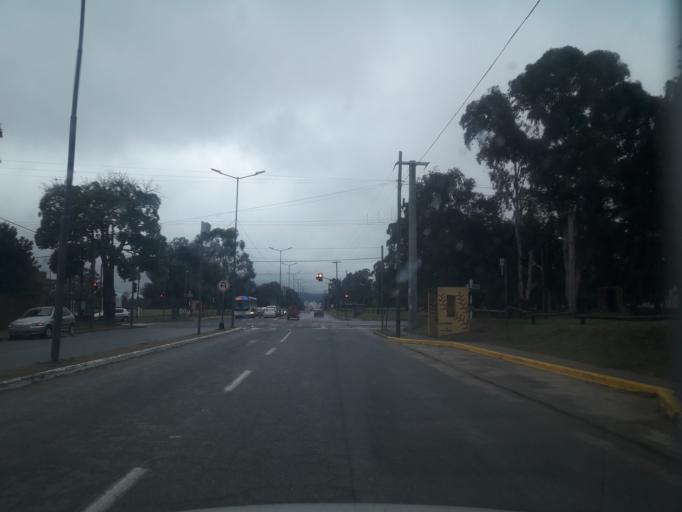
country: AR
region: Buenos Aires
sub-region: Partido de Tandil
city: Tandil
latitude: -37.3046
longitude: -59.1652
